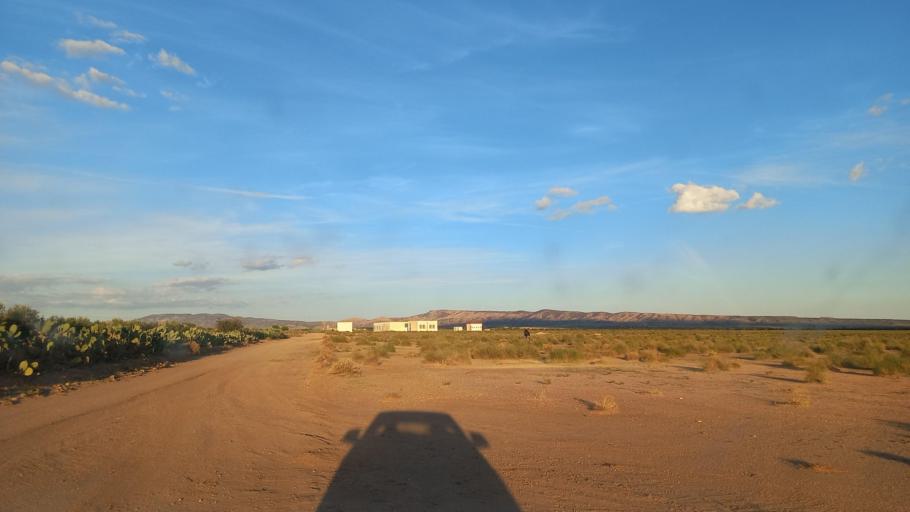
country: TN
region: Al Qasrayn
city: Sbiba
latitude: 35.3489
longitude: 9.0360
